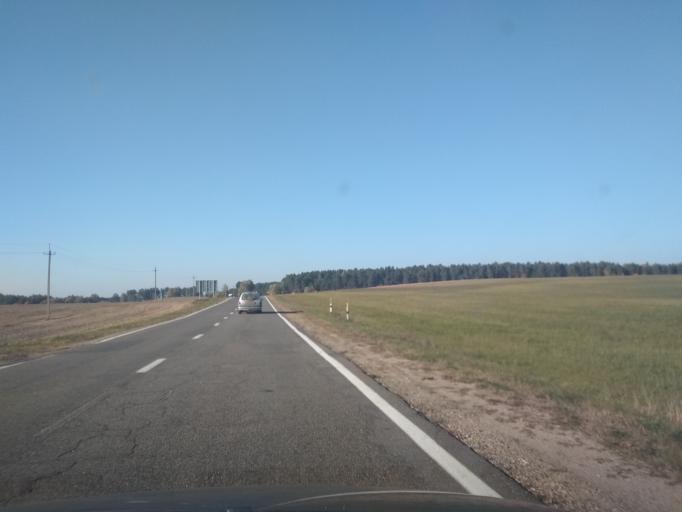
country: BY
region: Grodnenskaya
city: Vawkavysk
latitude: 53.1470
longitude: 24.5031
